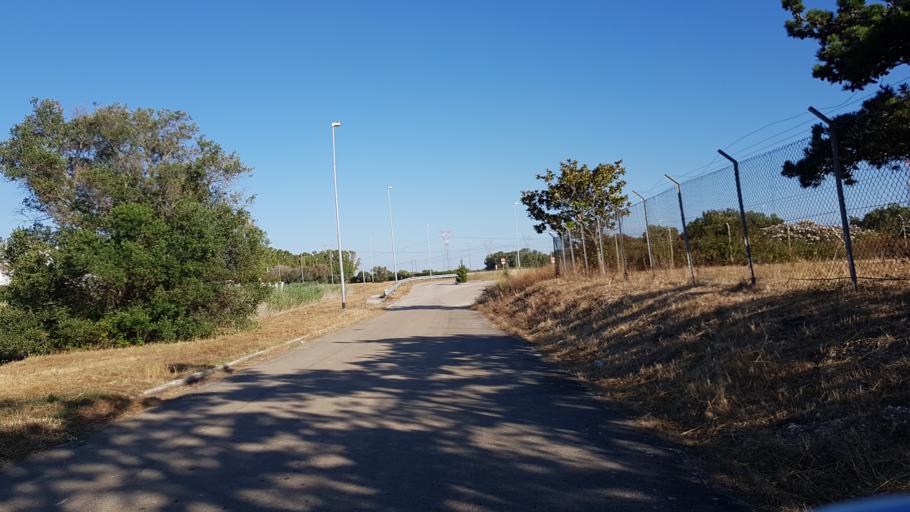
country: IT
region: Apulia
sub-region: Provincia di Brindisi
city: Tuturano
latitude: 40.5603
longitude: 18.0199
